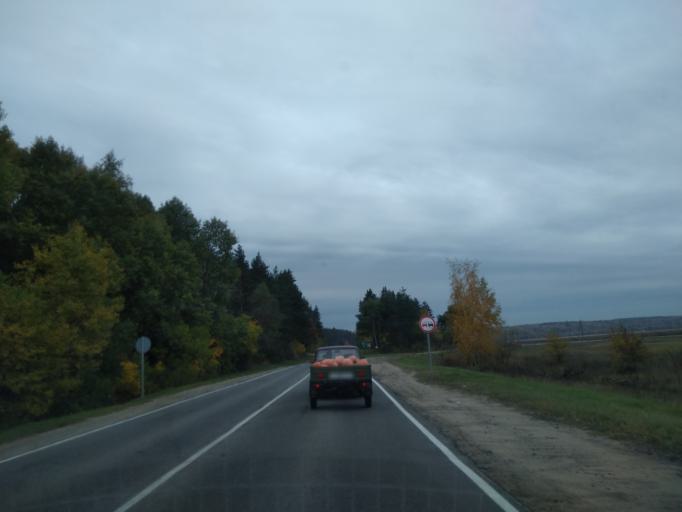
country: RU
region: Lipetsk
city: Zadonsk
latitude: 52.3657
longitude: 38.9166
